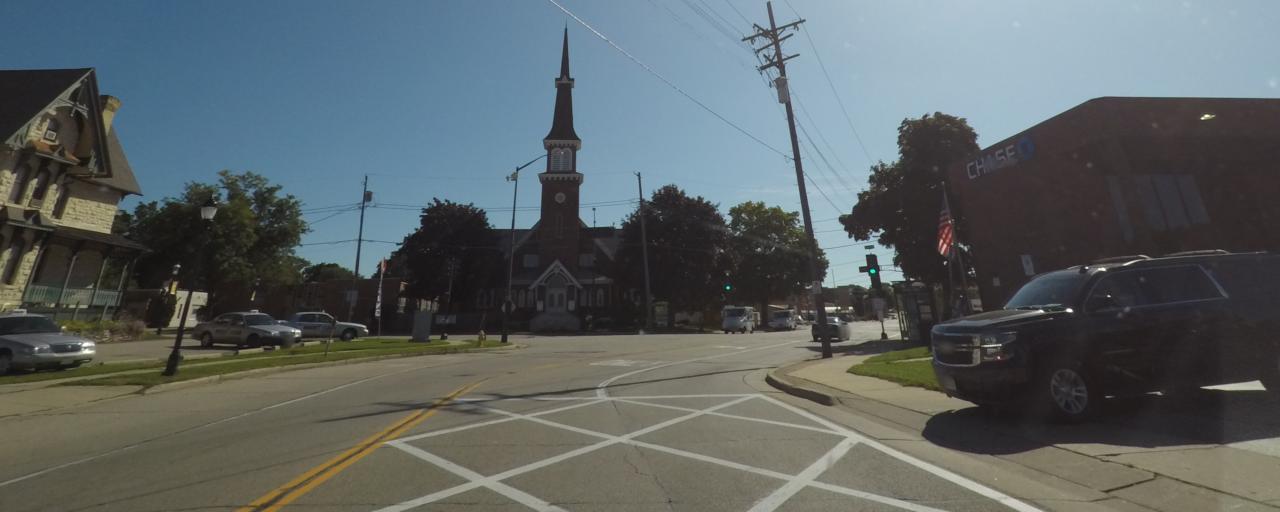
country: US
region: Wisconsin
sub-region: Waukesha County
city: Waukesha
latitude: 43.0098
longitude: -88.2273
